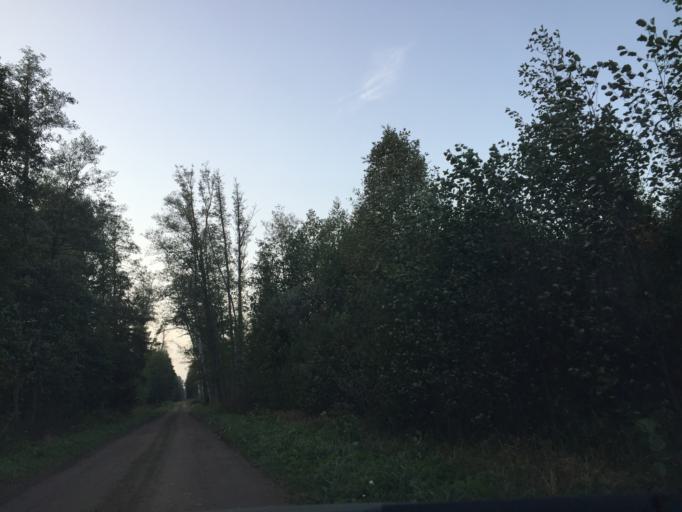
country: LV
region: Ikskile
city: Ikskile
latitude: 56.9322
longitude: 24.4861
